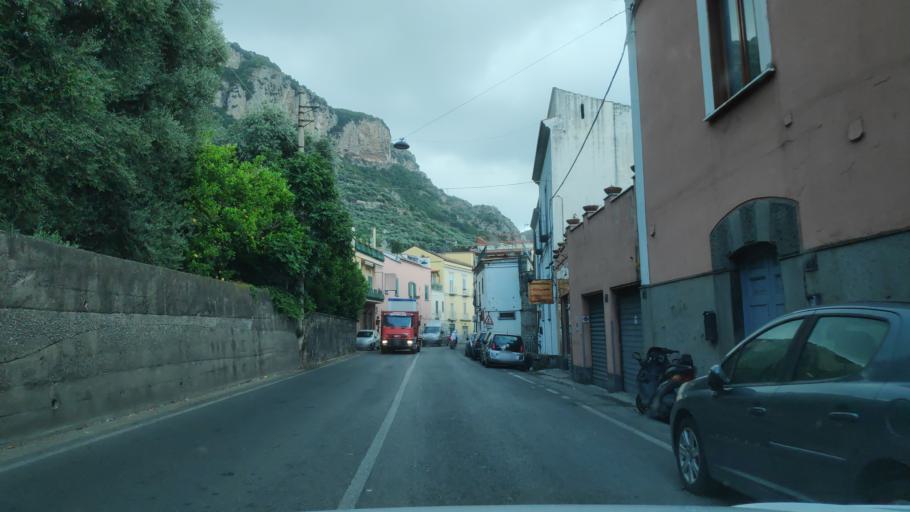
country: IT
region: Campania
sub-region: Provincia di Napoli
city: Meta
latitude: 40.6436
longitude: 14.4163
